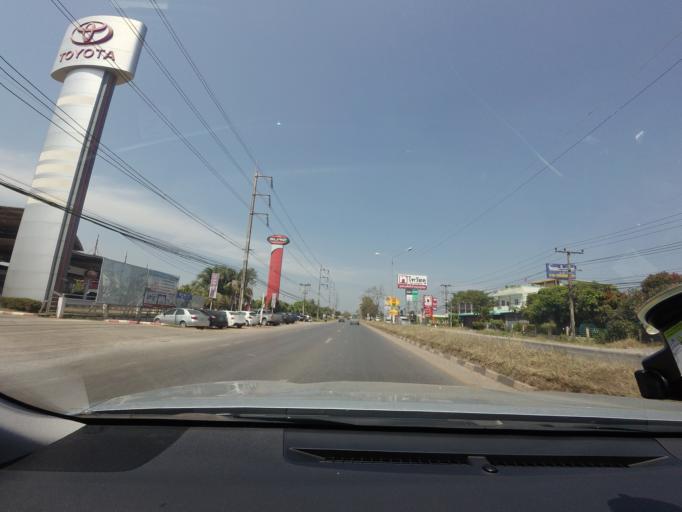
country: TH
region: Surat Thani
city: Surat Thani
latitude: 9.1473
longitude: 99.4001
